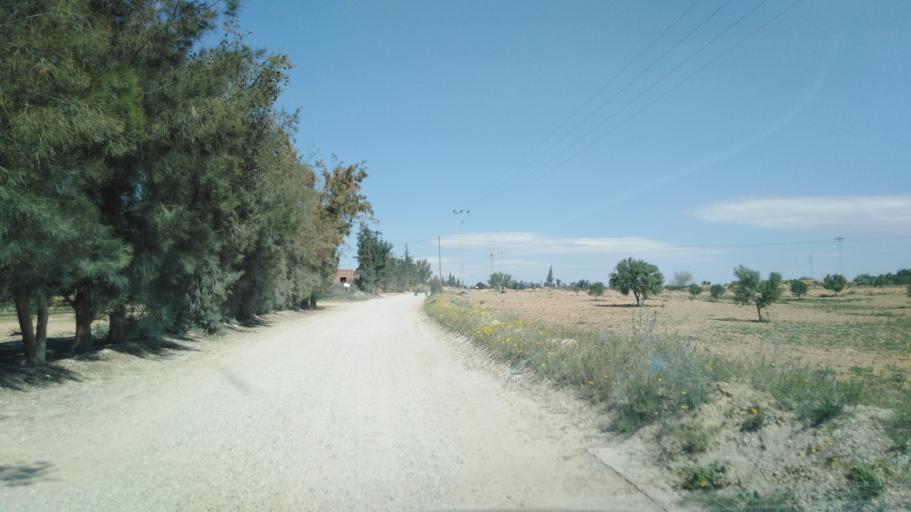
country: TN
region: Safaqis
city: Sfax
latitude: 34.7570
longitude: 10.5294
